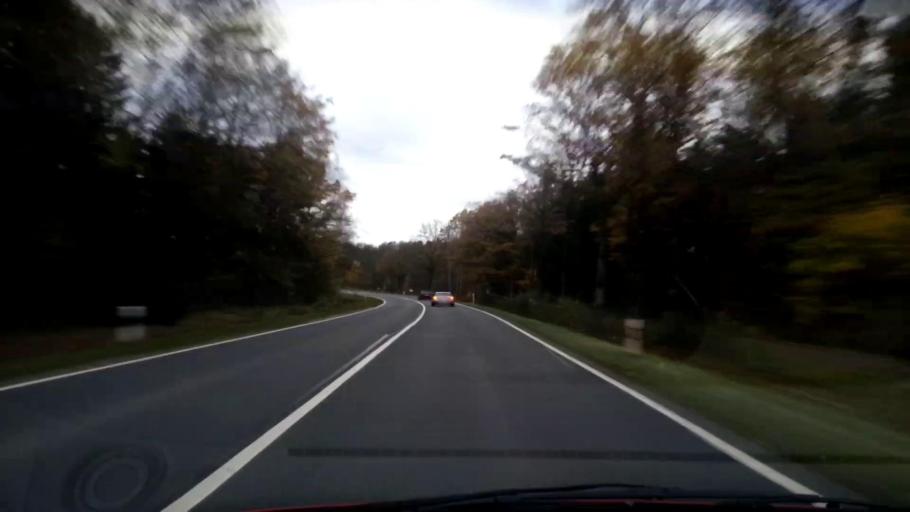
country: DE
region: Bavaria
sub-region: Upper Franconia
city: Sonnefeld
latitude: 50.2197
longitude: 11.1084
